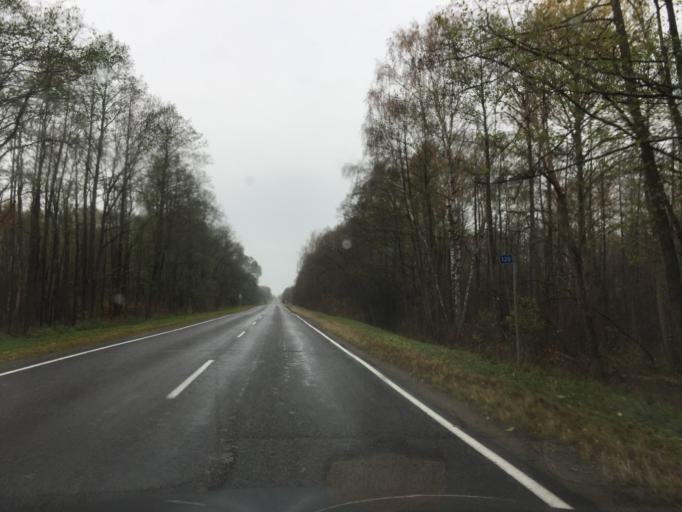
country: BY
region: Gomel
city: Karma
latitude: 53.3161
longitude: 30.7534
